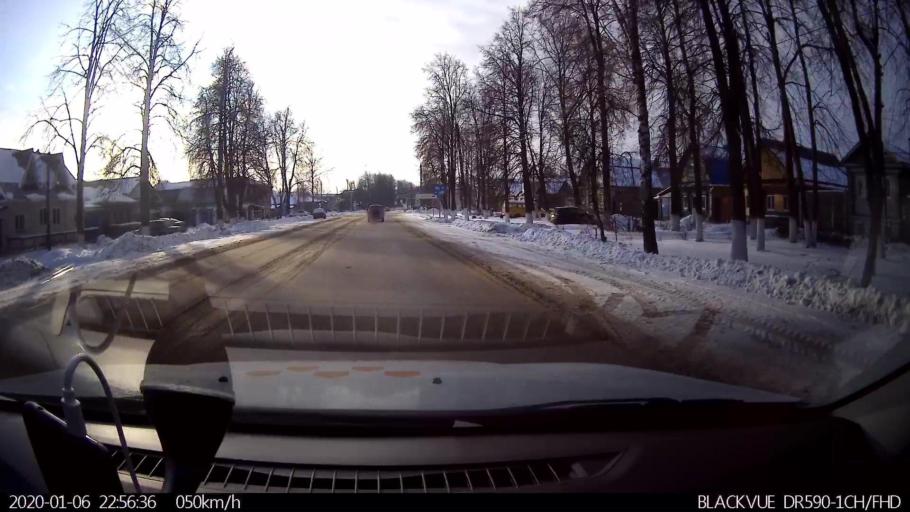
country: RU
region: Nizjnij Novgorod
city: Bogorodsk
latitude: 56.1103
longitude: 43.5300
